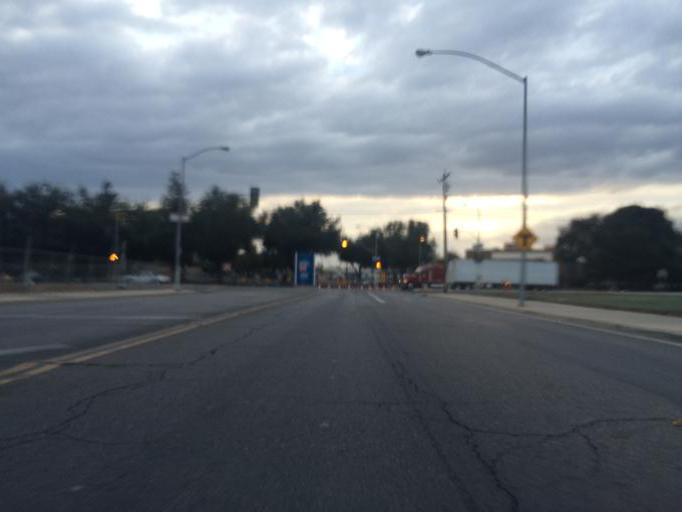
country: US
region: California
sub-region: Fresno County
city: Fresno
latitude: 36.7433
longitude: -119.8062
